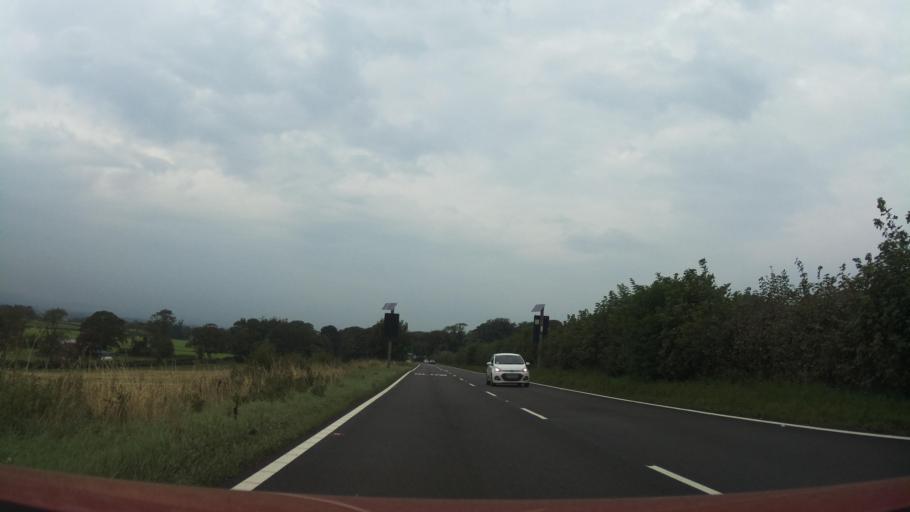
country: GB
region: Scotland
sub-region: Dumfries and Galloway
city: Lochmaben
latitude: 55.0566
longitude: -3.4723
